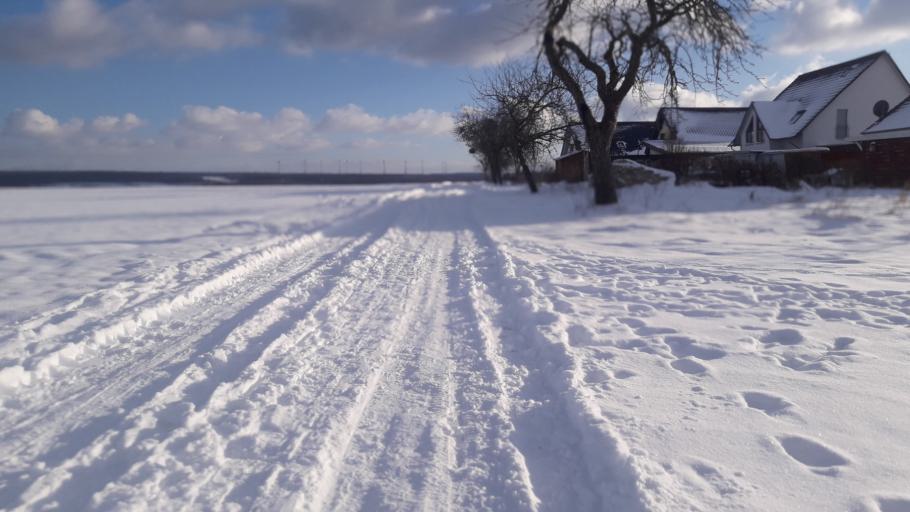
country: DE
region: North Rhine-Westphalia
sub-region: Regierungsbezirk Detmold
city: Salzkotten
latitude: 51.6437
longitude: 8.6732
